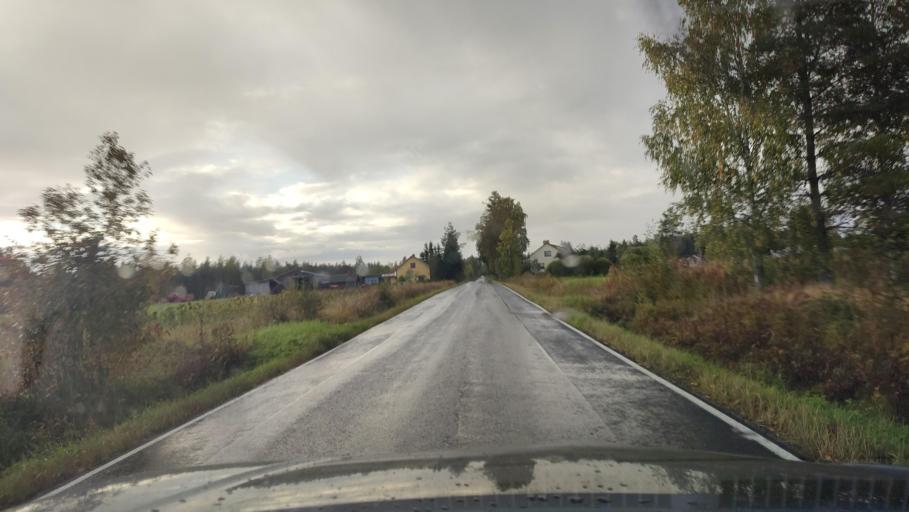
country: FI
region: Southern Ostrobothnia
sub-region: Suupohja
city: Karijoki
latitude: 62.3146
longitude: 21.6958
